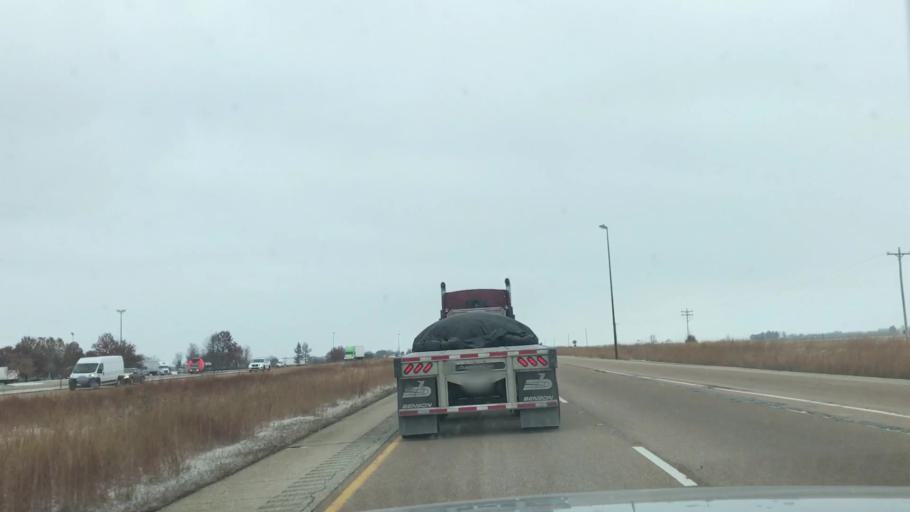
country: US
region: Illinois
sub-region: Montgomery County
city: Raymond
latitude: 39.3498
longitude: -89.6426
